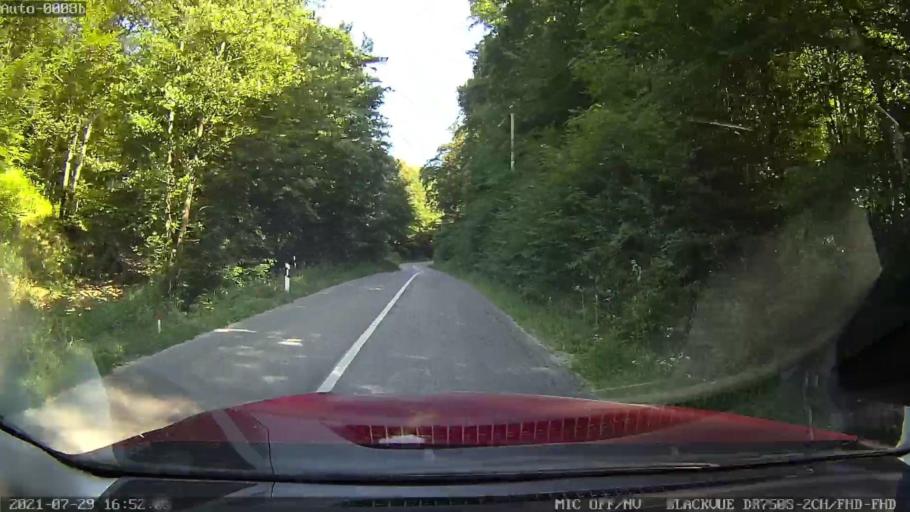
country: HR
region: Varazdinska
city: Ivanec
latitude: 46.2053
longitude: 16.1327
